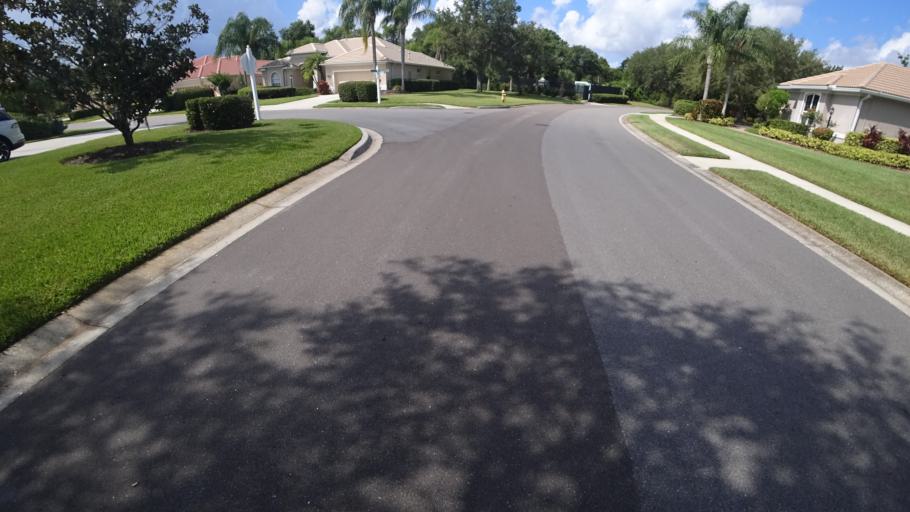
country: US
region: Florida
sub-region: Sarasota County
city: The Meadows
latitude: 27.4149
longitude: -82.4231
